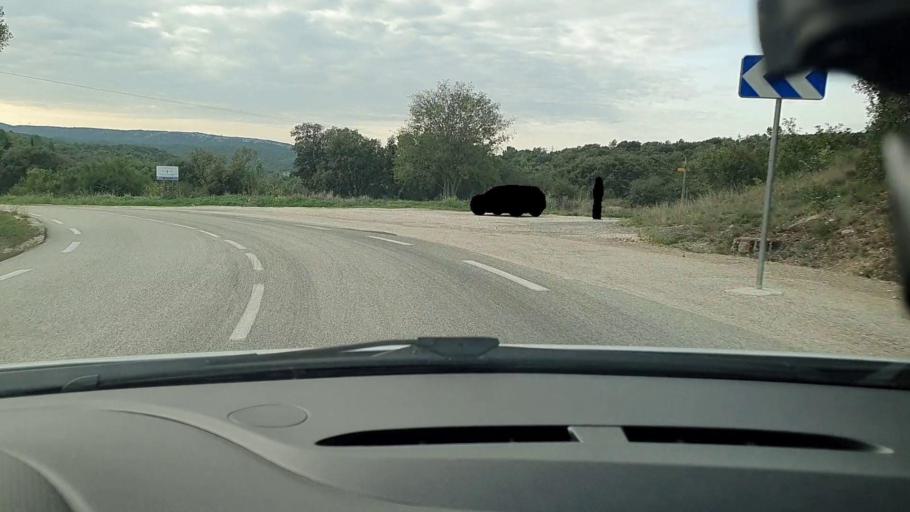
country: FR
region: Languedoc-Roussillon
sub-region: Departement du Gard
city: Mons
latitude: 44.1162
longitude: 4.2216
